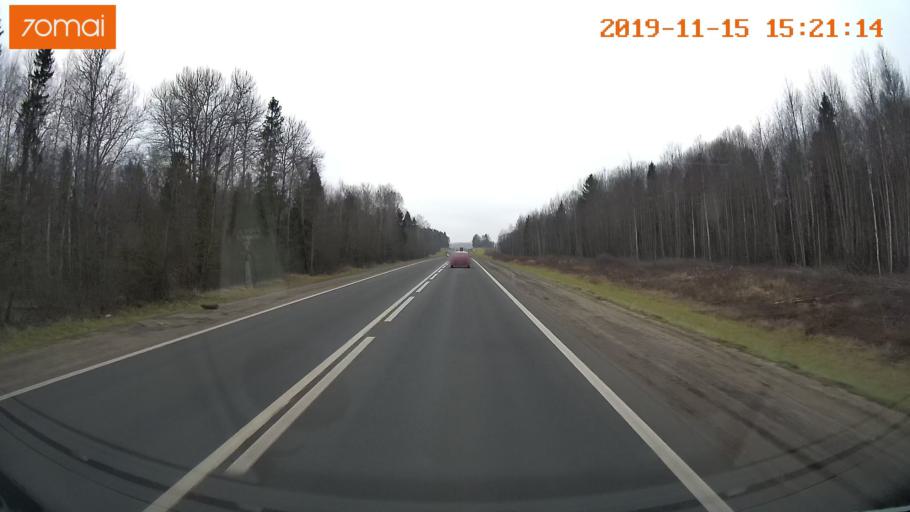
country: RU
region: Jaroslavl
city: Danilov
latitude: 58.2149
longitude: 40.1490
